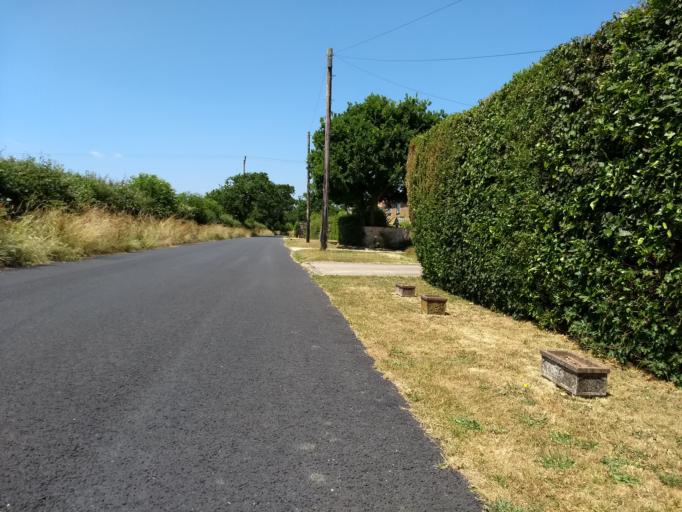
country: GB
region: England
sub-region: Isle of Wight
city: Shalfleet
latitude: 50.7153
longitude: -1.3643
